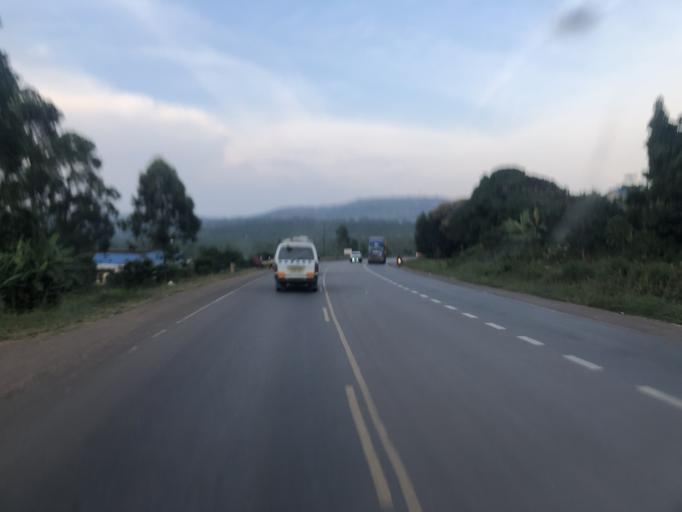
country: UG
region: Central Region
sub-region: Mpigi District
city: Mpigi
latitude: 0.2406
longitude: 32.3503
